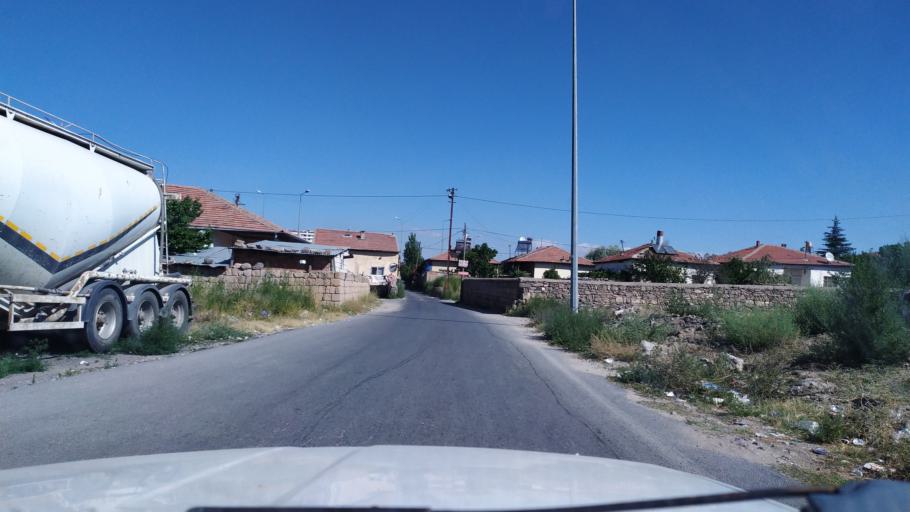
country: TR
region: Kayseri
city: Talas
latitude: 38.7203
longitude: 35.5503
